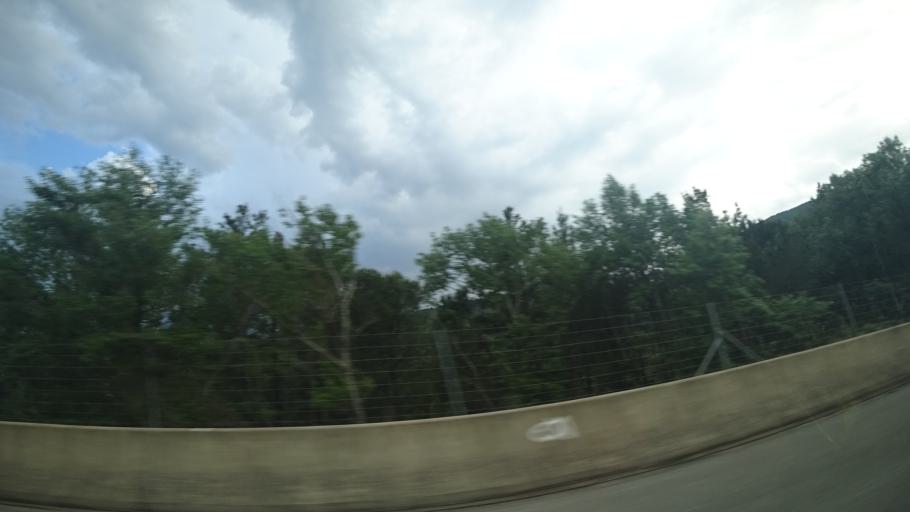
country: FR
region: Languedoc-Roussillon
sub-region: Departement de l'Herault
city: Lodeve
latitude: 43.7750
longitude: 3.3312
